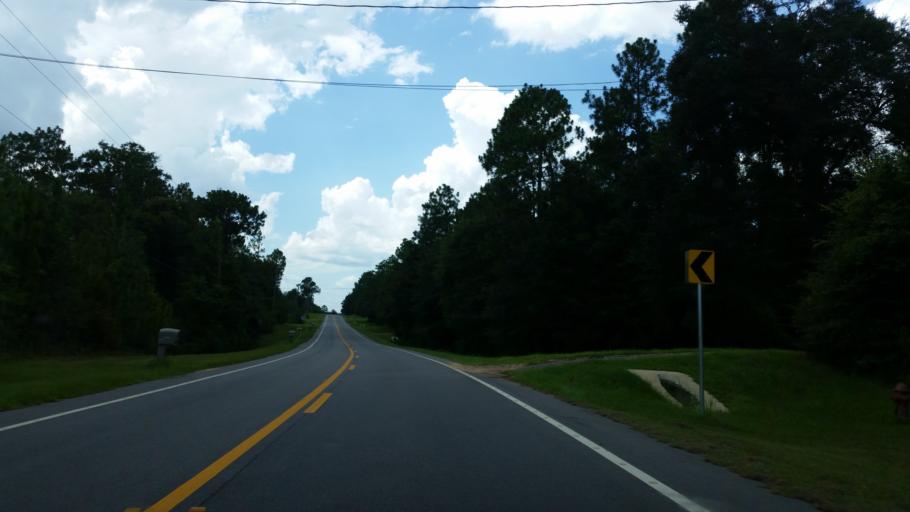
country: US
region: Florida
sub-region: Escambia County
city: Cantonment
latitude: 30.6616
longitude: -87.3868
